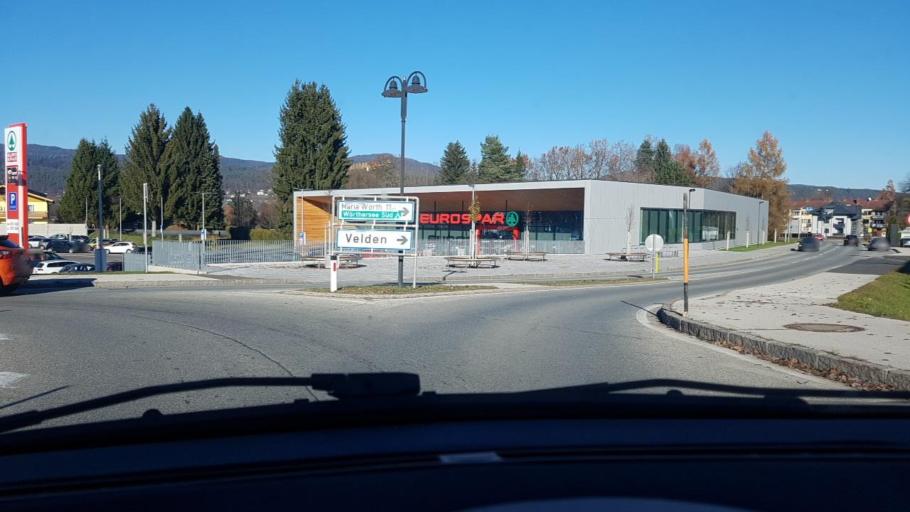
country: AT
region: Carinthia
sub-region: Politischer Bezirk Villach Land
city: Velden am Woerthersee
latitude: 46.6046
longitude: 14.0362
